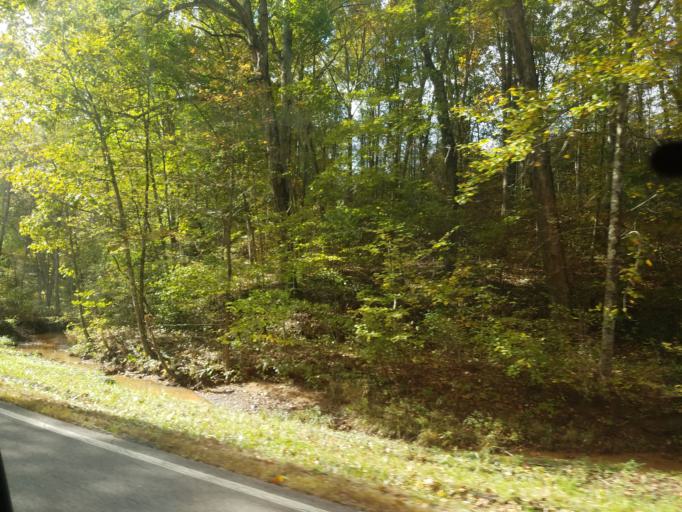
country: US
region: Ohio
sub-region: Vinton County
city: McArthur
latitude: 39.1641
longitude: -82.4355
